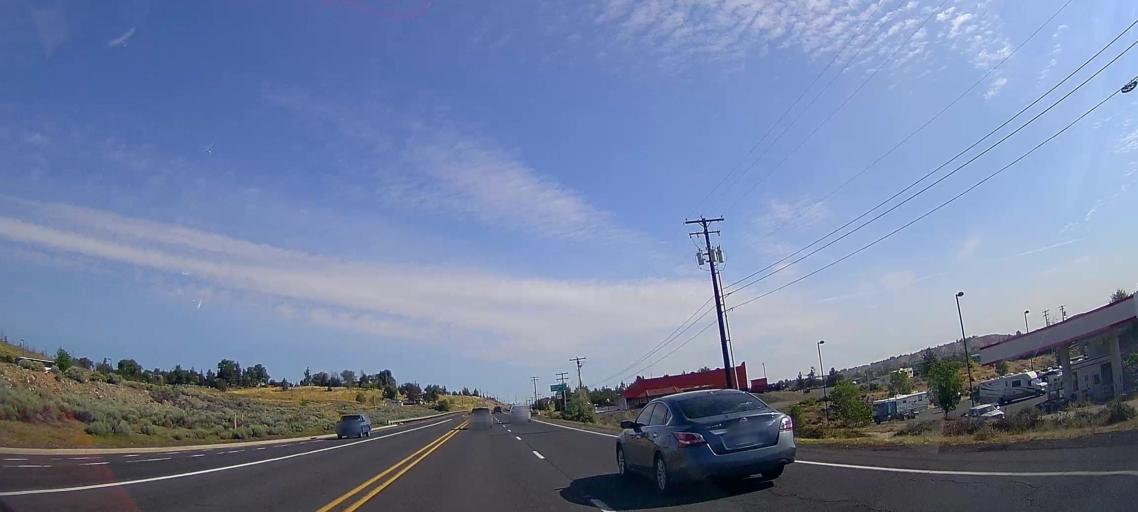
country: US
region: Oregon
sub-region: Jefferson County
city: Madras
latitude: 44.6436
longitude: -121.1295
